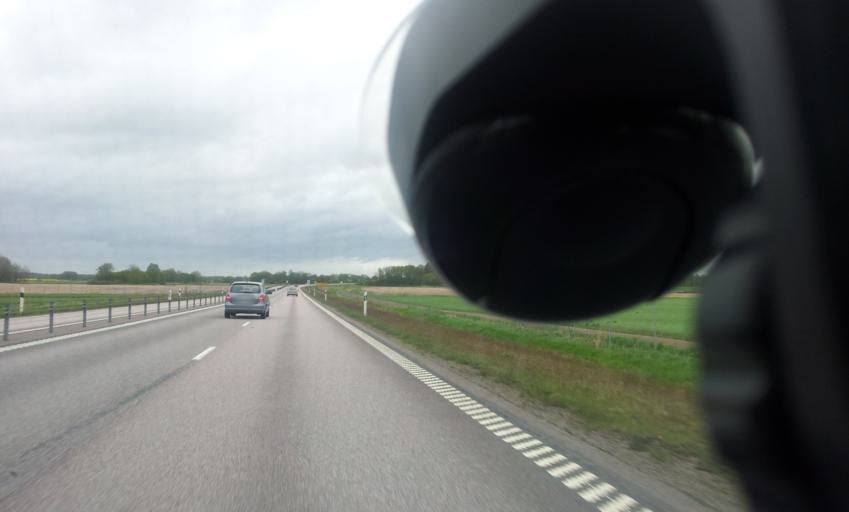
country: SE
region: Kalmar
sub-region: Kalmar Kommun
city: Ljungbyholm
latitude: 56.6045
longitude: 16.1337
